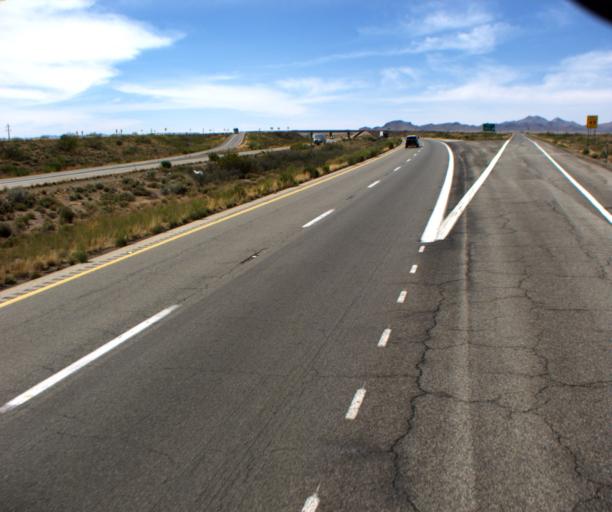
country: US
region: Arizona
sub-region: Cochise County
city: Willcox
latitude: 32.3602
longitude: -109.6155
